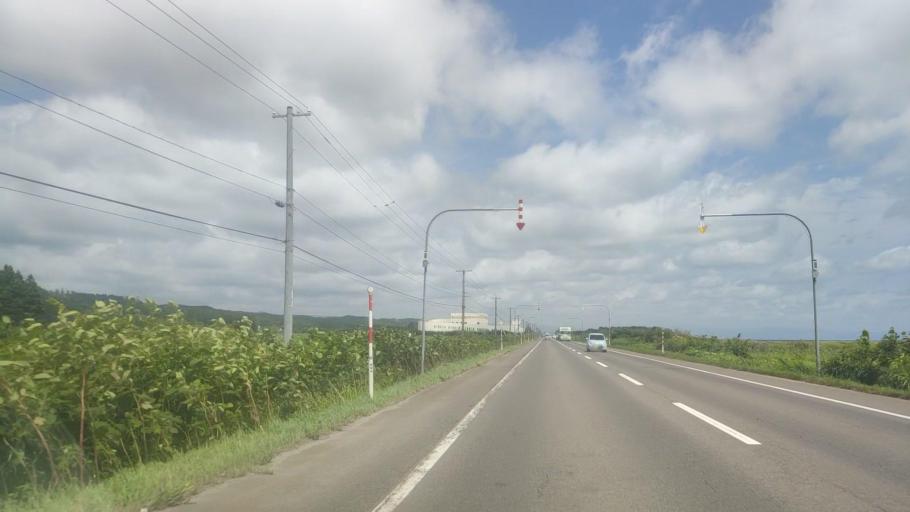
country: JP
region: Hokkaido
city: Niseko Town
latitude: 42.3818
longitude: 140.2940
